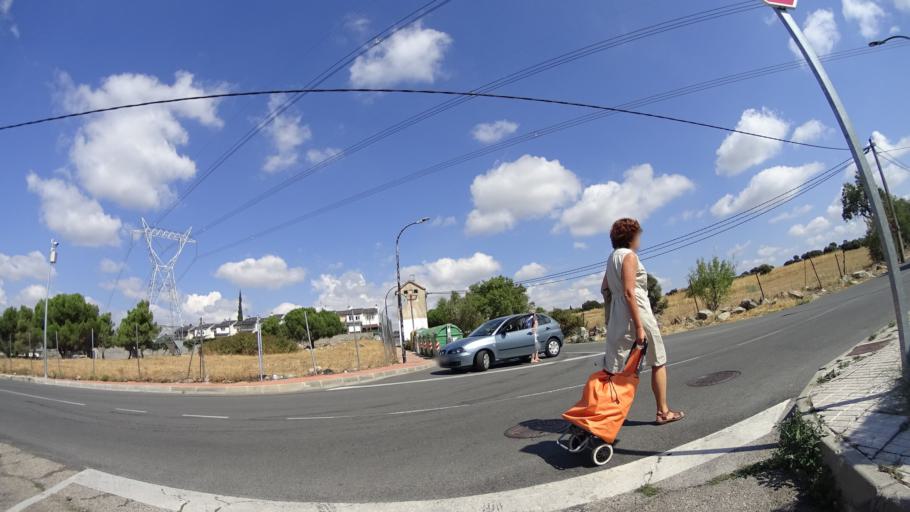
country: ES
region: Madrid
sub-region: Provincia de Madrid
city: Galapagar
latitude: 40.5825
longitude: -3.9942
